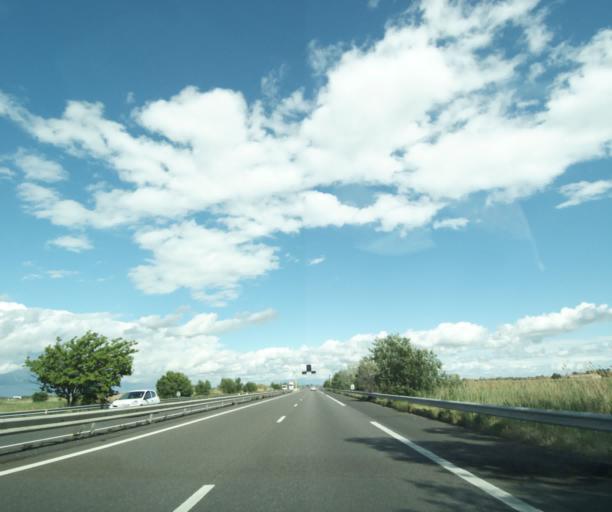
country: FR
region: Languedoc-Roussillon
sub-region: Departement du Gard
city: Bellegarde
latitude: 43.7303
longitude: 4.4892
